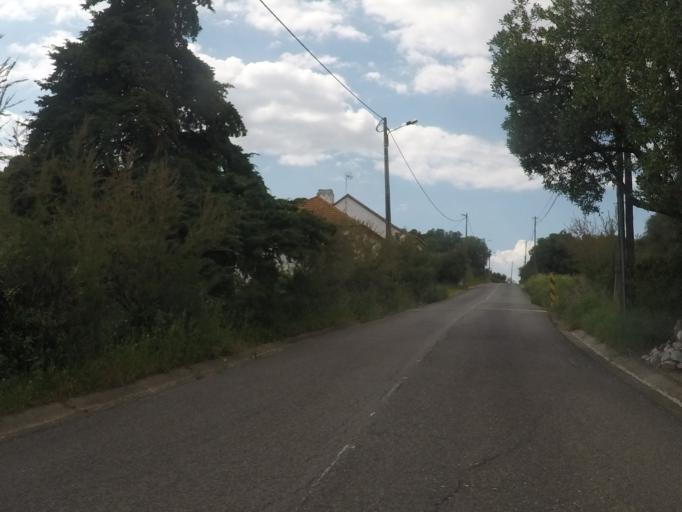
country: PT
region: Setubal
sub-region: Palmela
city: Quinta do Anjo
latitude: 38.5101
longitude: -9.0040
